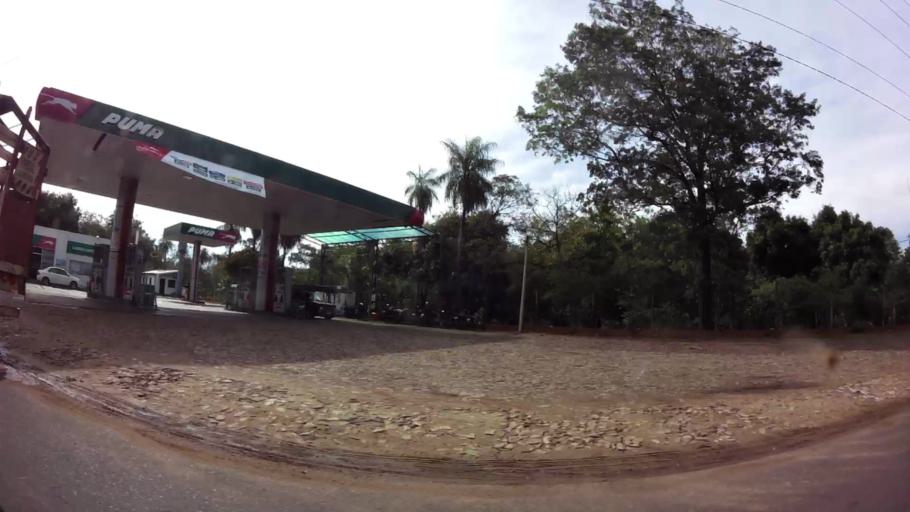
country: PY
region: Central
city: Limpio
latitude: -25.1649
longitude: -57.4676
